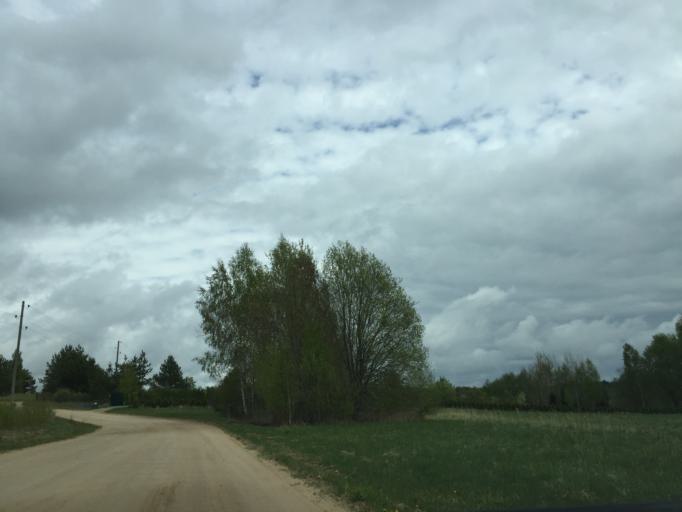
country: LV
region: Kekava
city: Kekava
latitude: 56.7910
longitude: 24.3073
